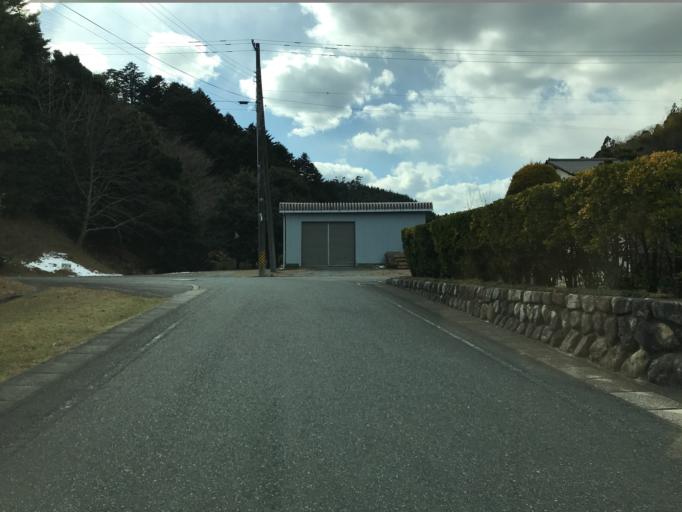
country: JP
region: Fukushima
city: Iwaki
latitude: 37.1683
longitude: 140.9986
